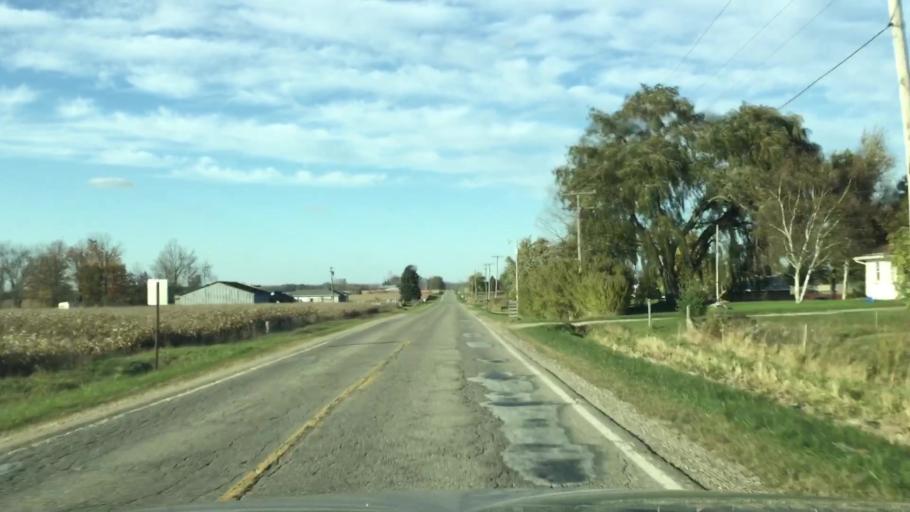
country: US
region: Michigan
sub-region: Lapeer County
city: North Branch
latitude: 43.2679
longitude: -83.1981
